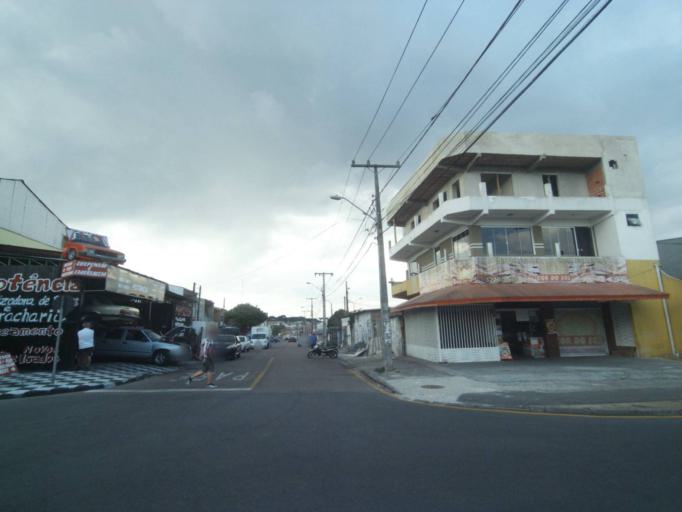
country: BR
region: Parana
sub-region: Sao Jose Dos Pinhais
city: Sao Jose dos Pinhais
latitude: -25.5326
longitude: -49.2719
